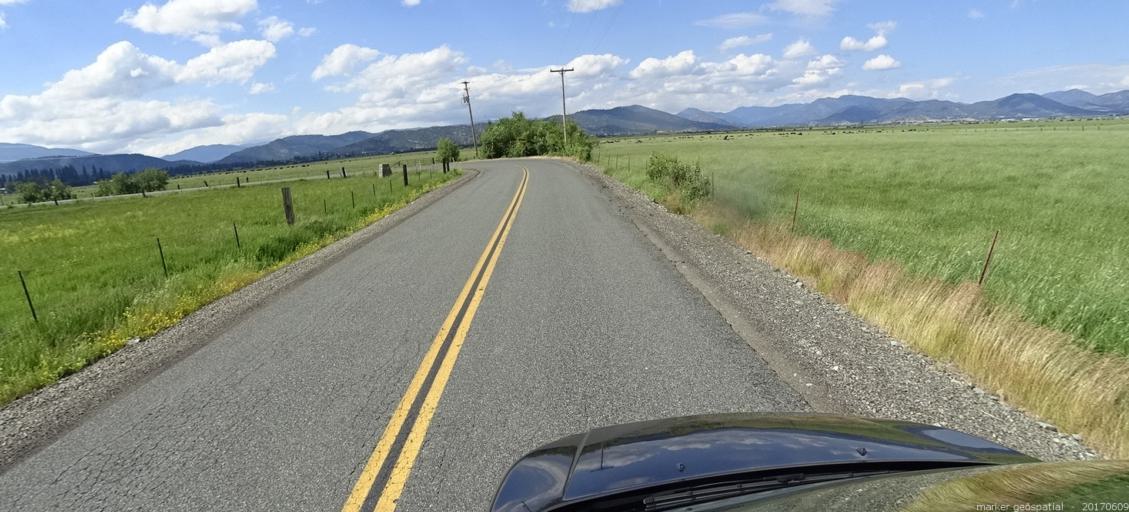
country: US
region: California
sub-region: Siskiyou County
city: Yreka
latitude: 41.5145
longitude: -122.8883
